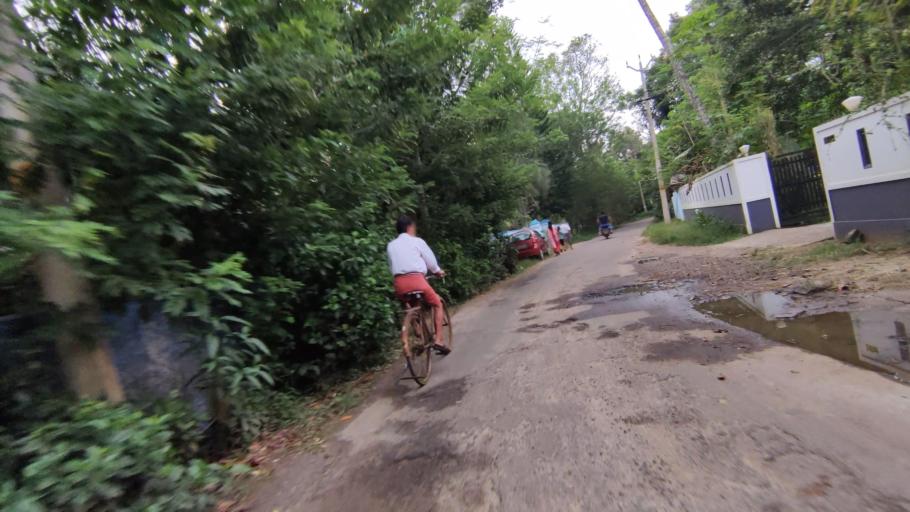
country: IN
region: Kerala
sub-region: Alappuzha
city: Shertallai
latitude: 9.6439
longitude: 76.3643
